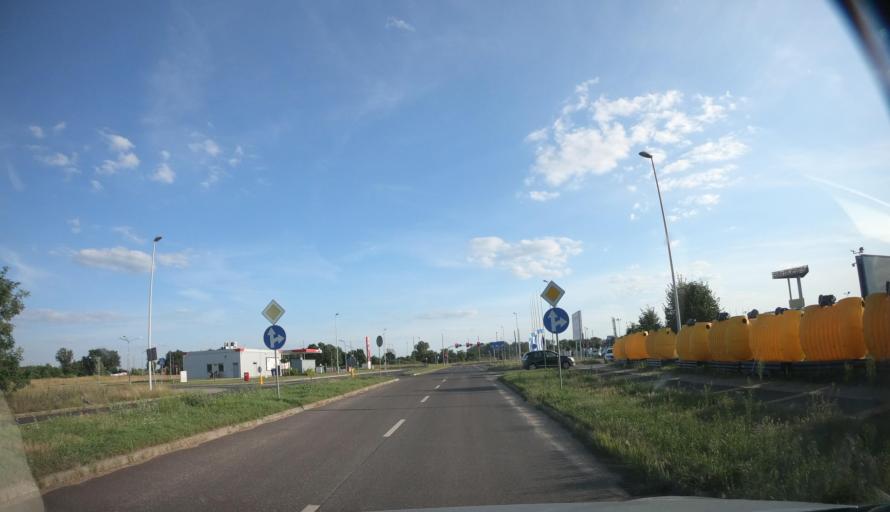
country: PL
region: Kujawsko-Pomorskie
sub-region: Powiat torunski
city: Wielka Nieszawka
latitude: 53.0178
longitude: 18.5358
